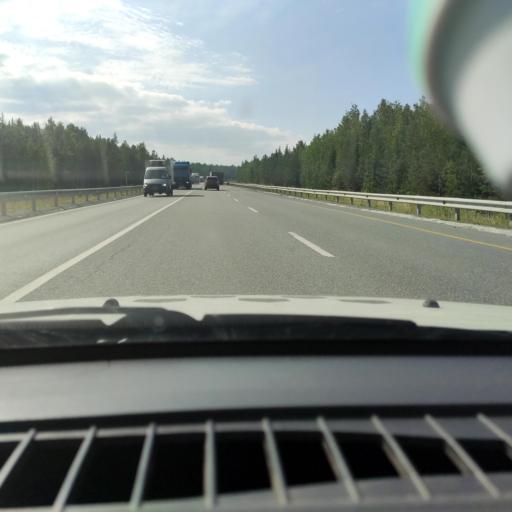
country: RU
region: Sverdlovsk
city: Revda
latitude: 56.8296
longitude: 59.8546
